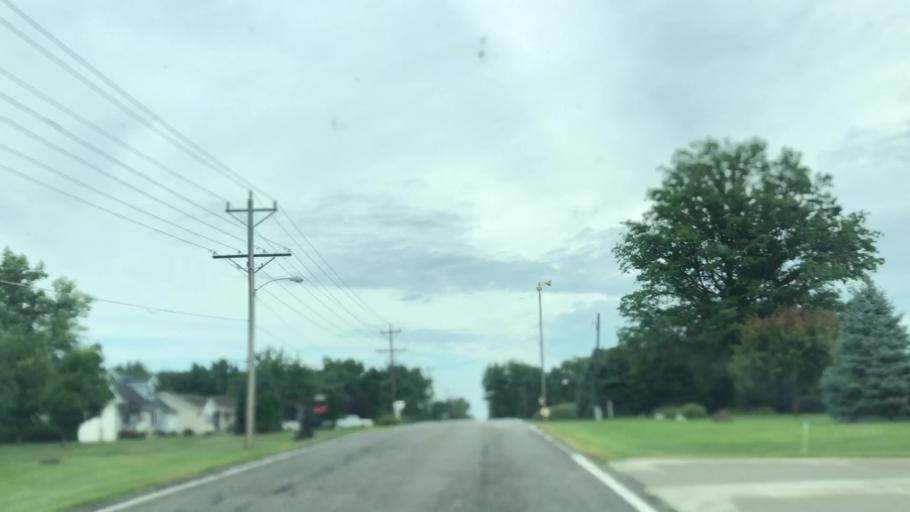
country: US
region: Iowa
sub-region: Marshall County
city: Marshalltown
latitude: 42.0391
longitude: -92.9610
